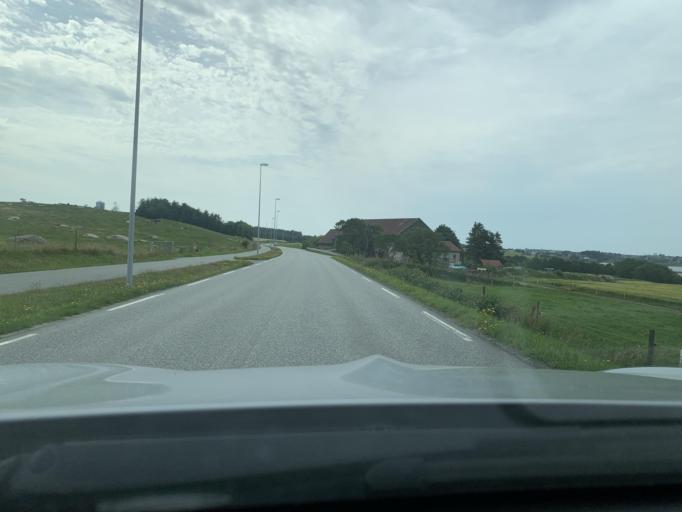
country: NO
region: Rogaland
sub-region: Time
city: Bryne
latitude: 58.7474
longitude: 5.6920
